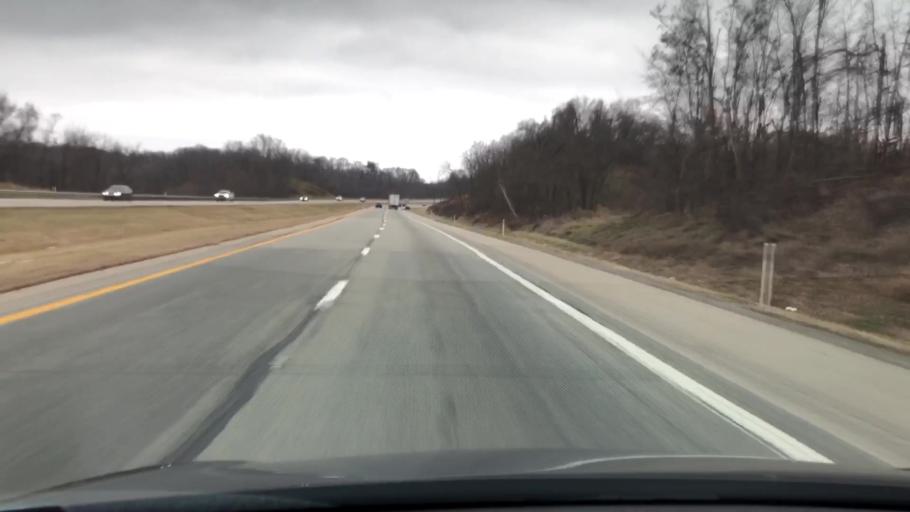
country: US
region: Pennsylvania
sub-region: Greene County
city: Morrisville
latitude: 39.8682
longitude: -80.1298
